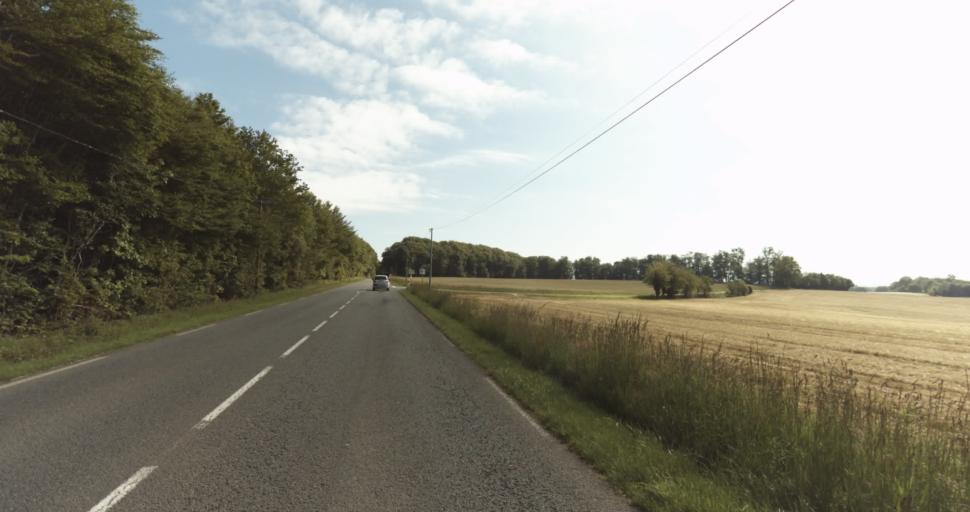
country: FR
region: Limousin
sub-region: Departement de la Haute-Vienne
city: Solignac
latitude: 45.7206
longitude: 1.2536
